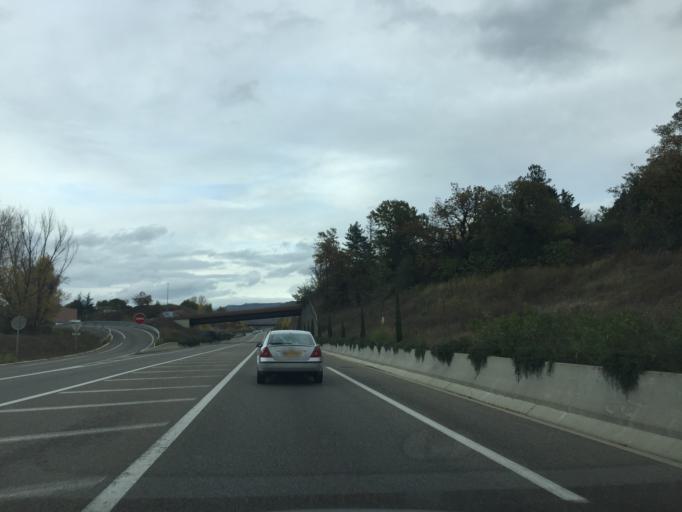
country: FR
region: Rhone-Alpes
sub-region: Departement de l'Ardeche
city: Saint-Etienne-de-Fontbellon
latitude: 44.6047
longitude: 4.3998
